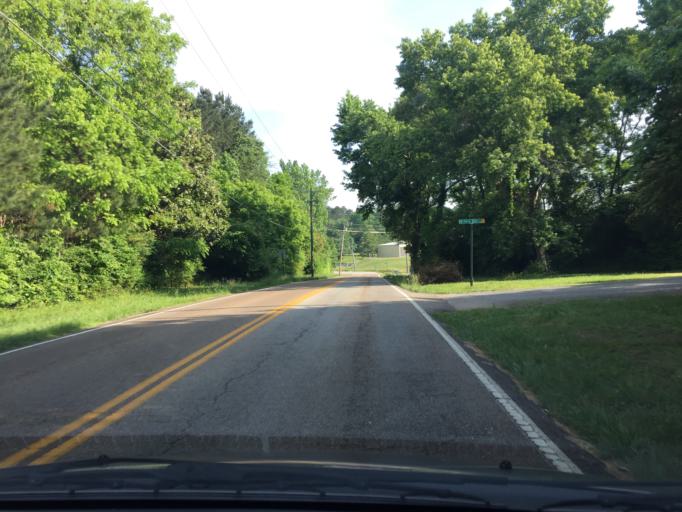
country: US
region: Tennessee
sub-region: Hamilton County
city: Apison
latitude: 35.0352
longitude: -85.0253
